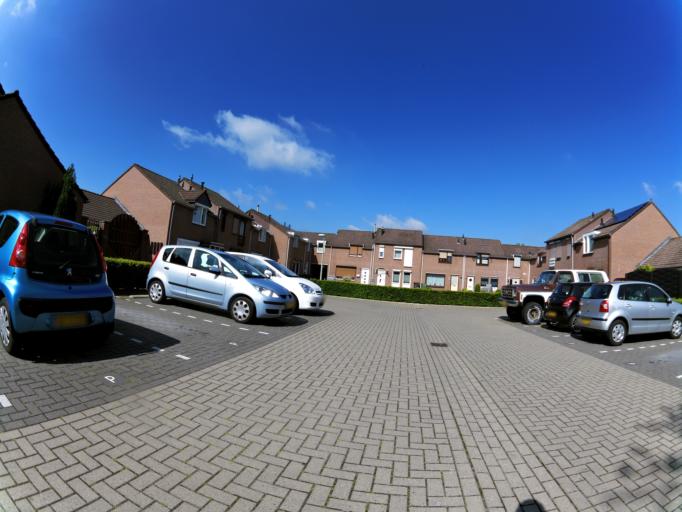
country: NL
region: Limburg
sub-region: Gemeente Heerlen
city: Heerlen
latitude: 50.8836
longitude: 6.0151
